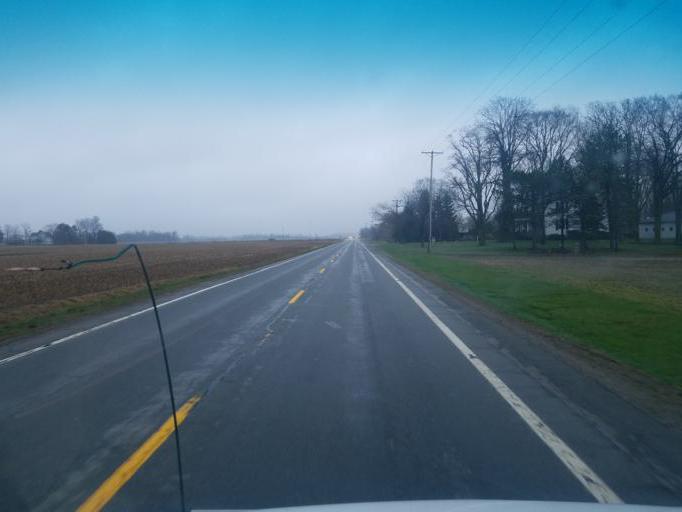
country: US
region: Ohio
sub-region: Wood County
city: Weston
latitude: 41.3723
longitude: -83.7710
